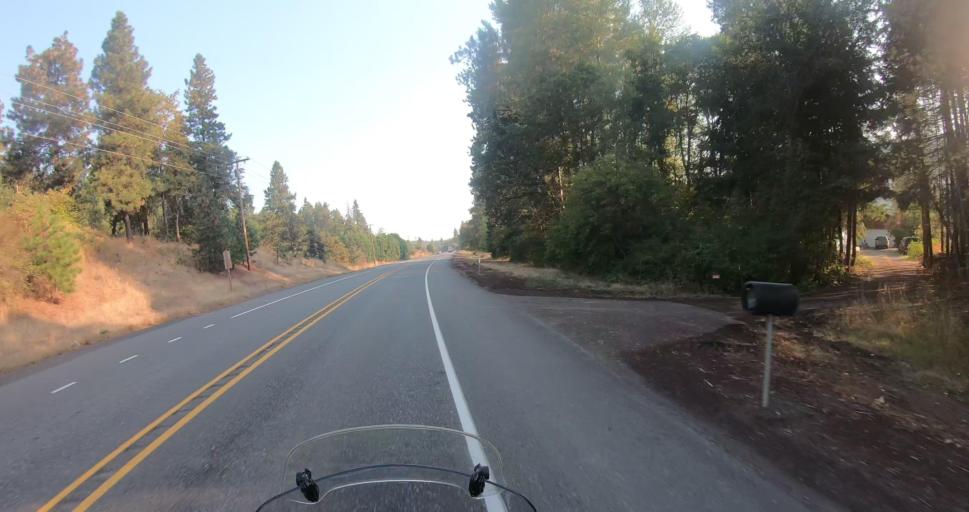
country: US
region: Oregon
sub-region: Hood River County
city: Odell
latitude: 45.5581
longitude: -121.5667
